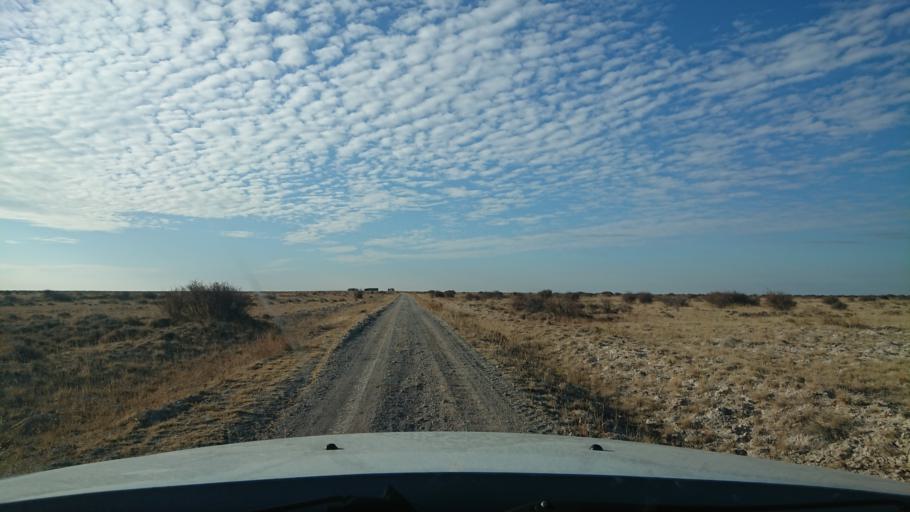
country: TR
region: Aksaray
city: Eskil
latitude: 38.5441
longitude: 33.3260
